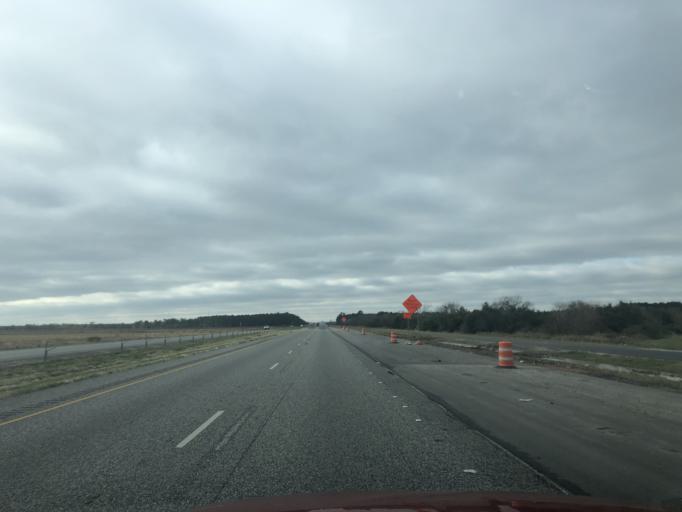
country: US
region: Texas
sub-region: Jefferson County
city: Fannett
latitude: 29.8986
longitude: -94.3094
